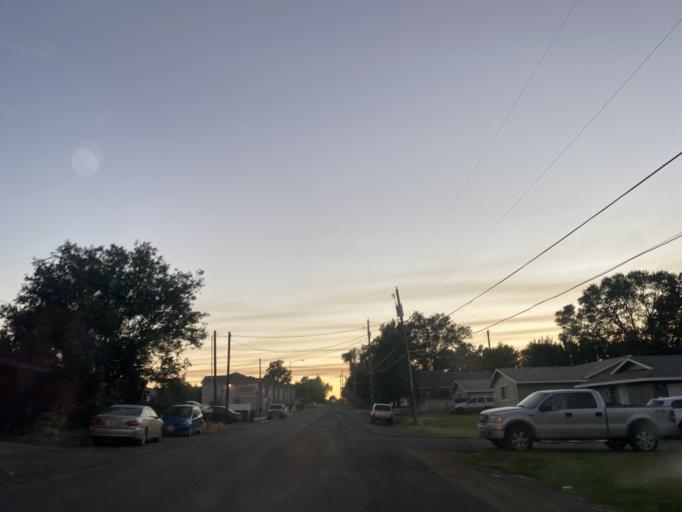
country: US
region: Washington
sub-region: Benton County
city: Kennewick
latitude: 46.2027
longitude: -119.1712
